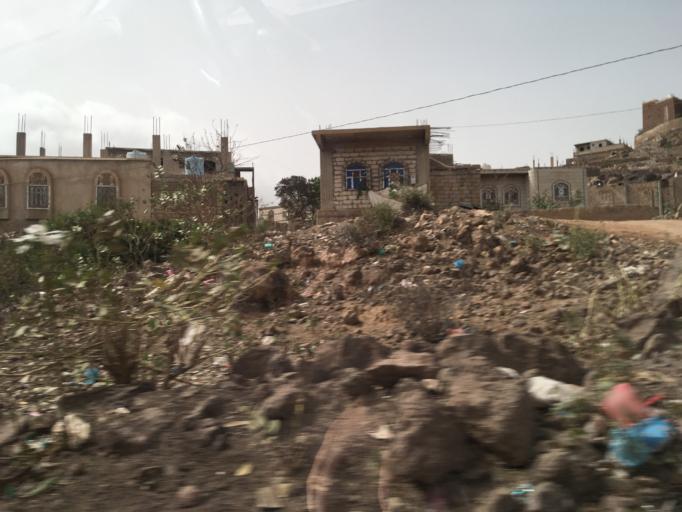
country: YE
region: Ad Dali'
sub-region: Ad Dhale'e
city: Dhalie
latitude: 13.6972
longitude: 44.7334
